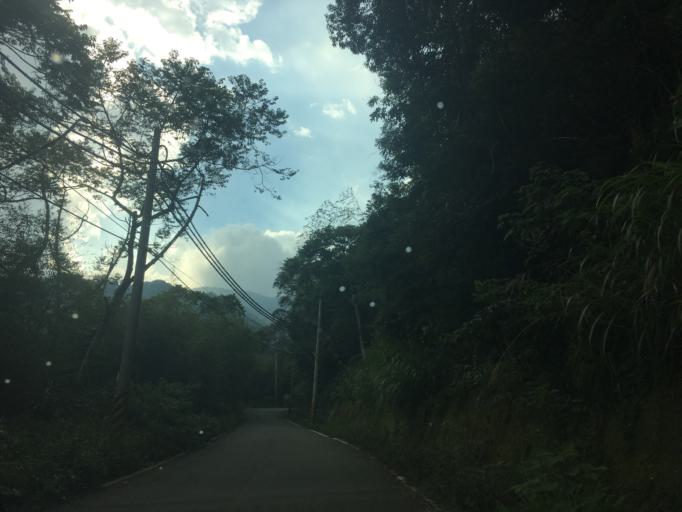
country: TW
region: Taiwan
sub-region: Miaoli
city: Miaoli
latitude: 24.3910
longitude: 120.9757
